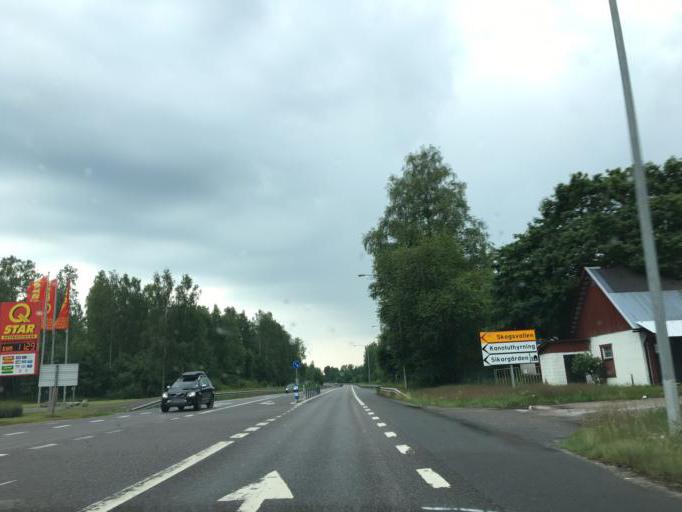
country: SE
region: OEstergoetland
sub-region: Norrkopings Kommun
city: Jursla
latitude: 58.7887
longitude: 16.1566
